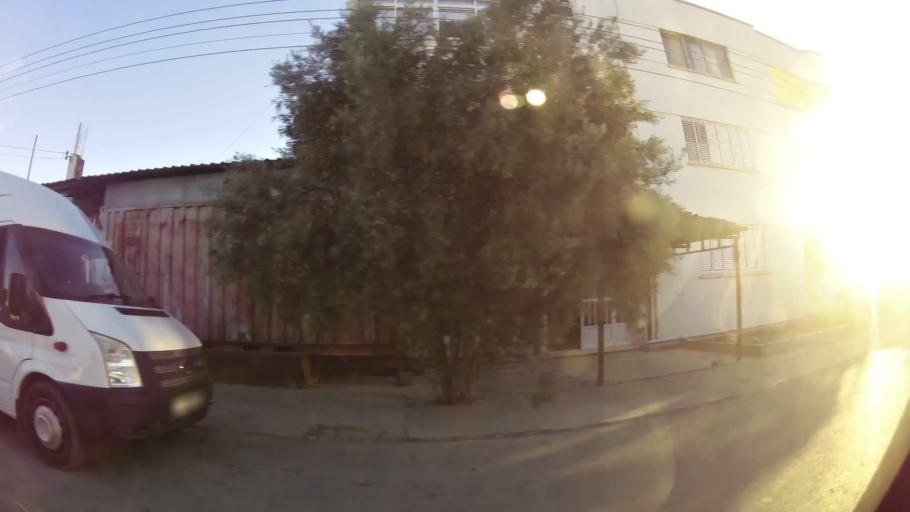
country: CY
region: Lefkosia
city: Nicosia
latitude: 35.2074
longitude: 33.3210
